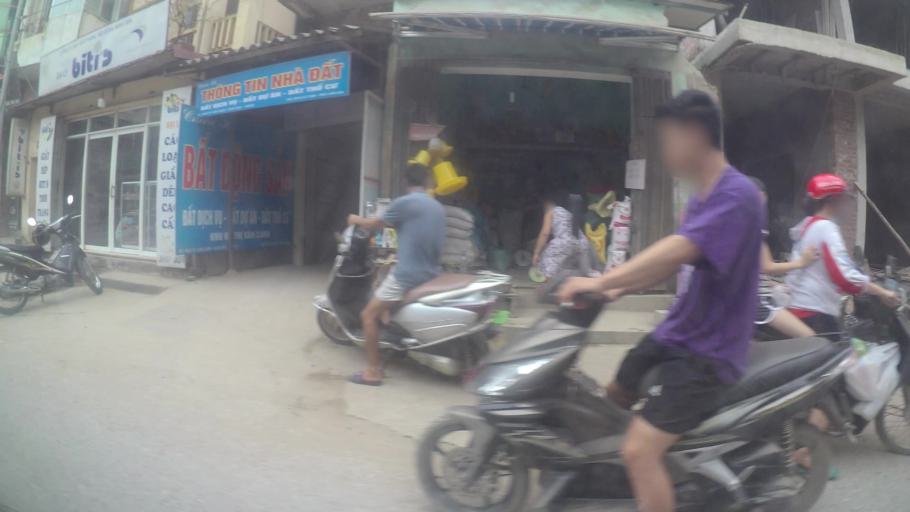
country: VN
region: Ha Noi
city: Cau Dien
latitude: 21.0348
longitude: 105.7363
